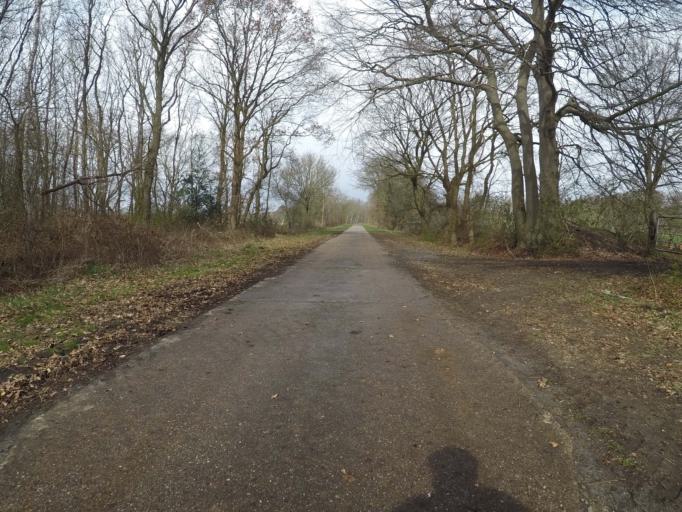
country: DE
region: Lower Saxony
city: Elmlohe
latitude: 53.6016
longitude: 8.6915
